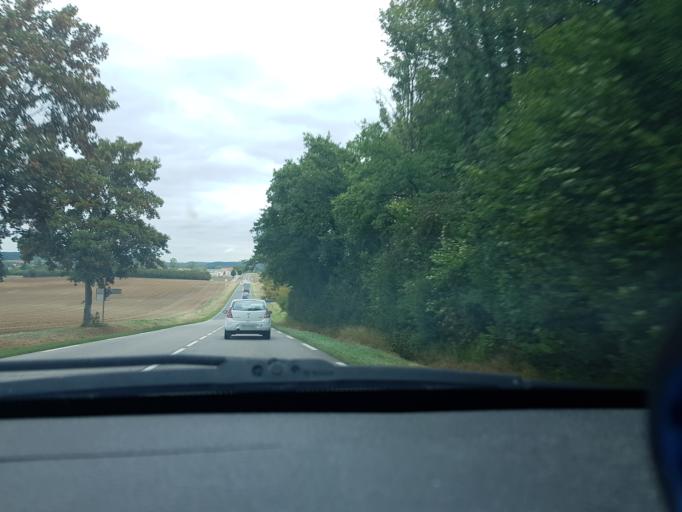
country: FR
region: Lorraine
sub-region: Departement de la Moselle
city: Chateau-Salins
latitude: 48.7730
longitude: 6.4508
